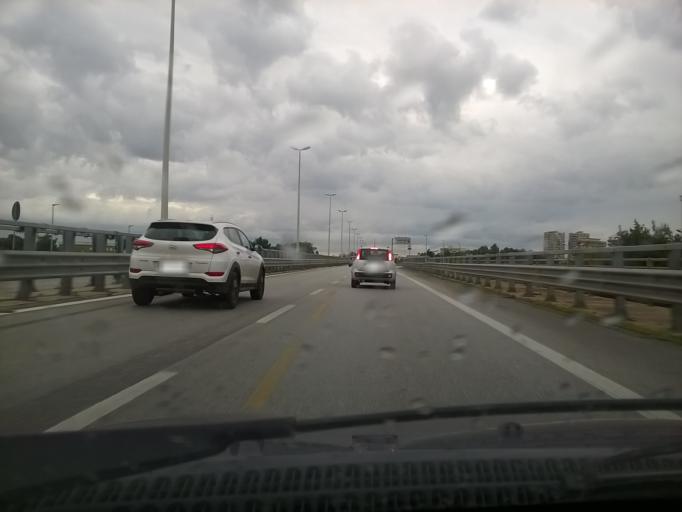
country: IT
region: Apulia
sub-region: Provincia di Taranto
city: Paolo VI
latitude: 40.4716
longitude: 17.2730
